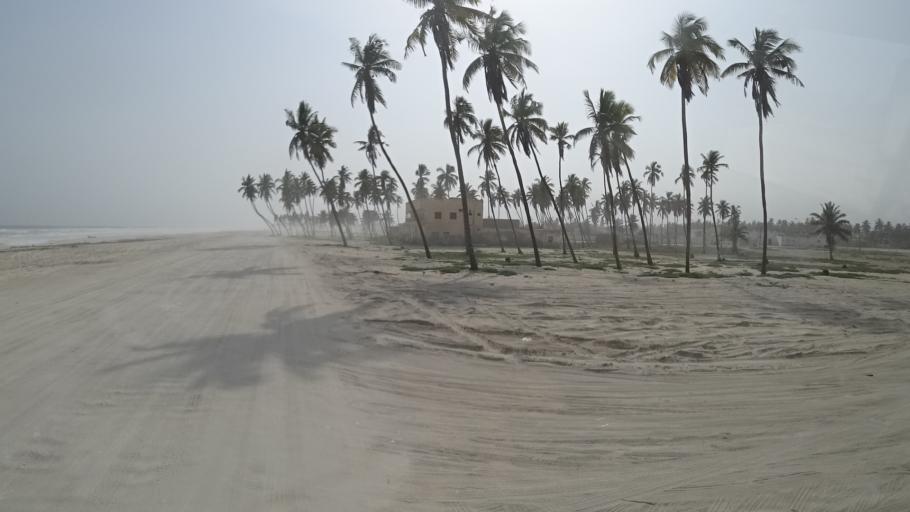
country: OM
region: Zufar
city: Salalah
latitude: 17.0013
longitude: 54.1129
